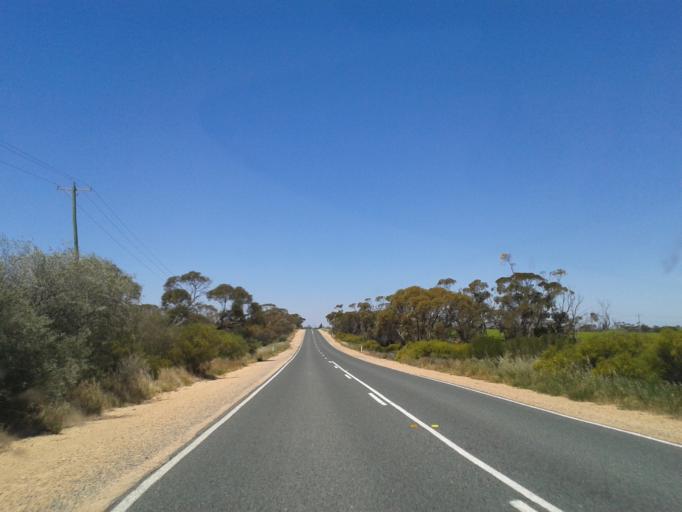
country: AU
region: Victoria
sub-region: Mildura Shire
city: Ouyen
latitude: -34.6930
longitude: 142.8665
